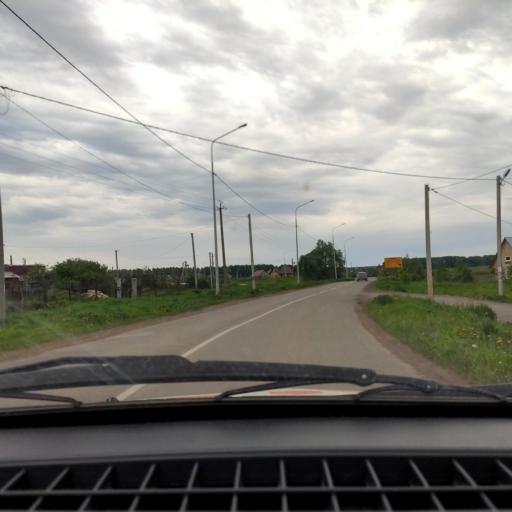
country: RU
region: Bashkortostan
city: Avdon
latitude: 54.5459
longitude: 55.7607
